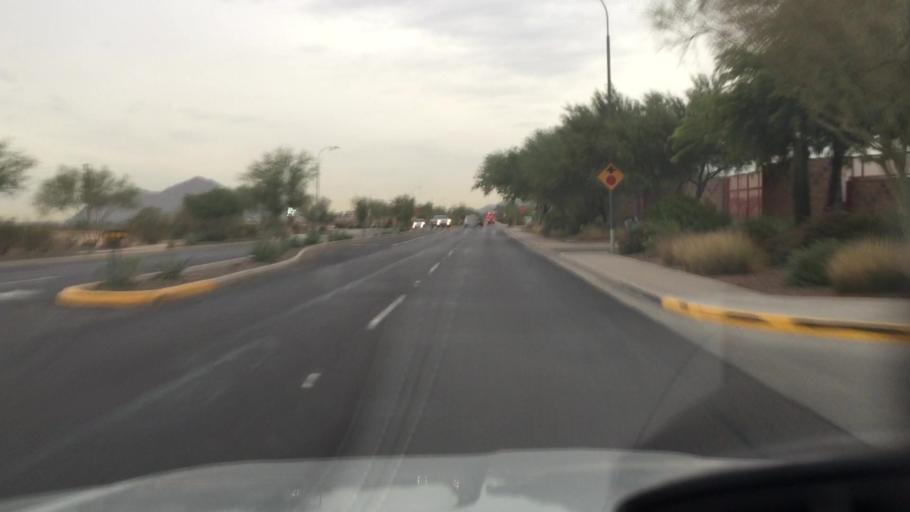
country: US
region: Arizona
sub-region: Maricopa County
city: Scottsdale
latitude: 33.5386
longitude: -111.8726
